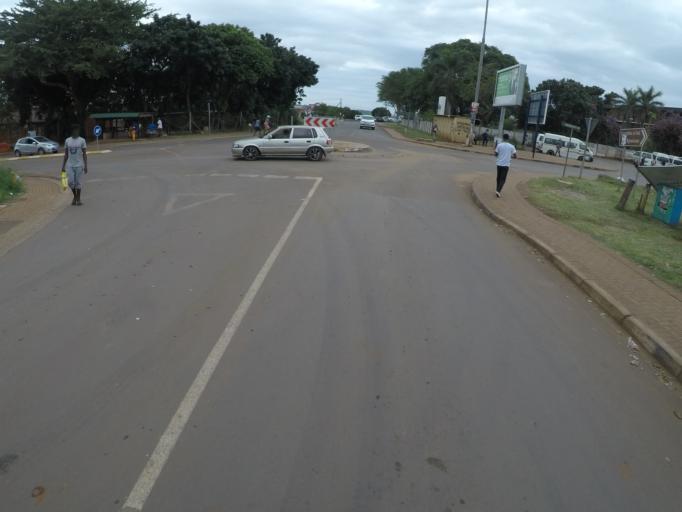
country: ZA
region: KwaZulu-Natal
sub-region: uThungulu District Municipality
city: Empangeni
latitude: -28.7737
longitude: 31.8633
